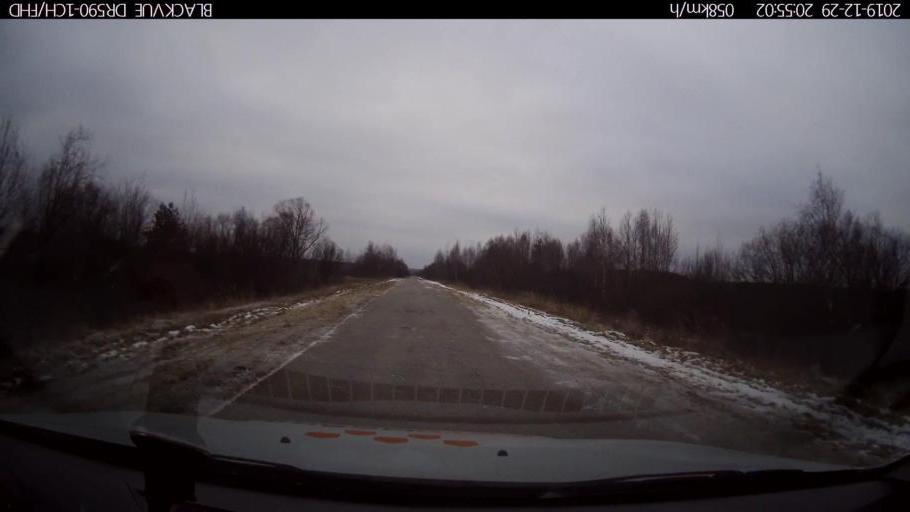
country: RU
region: Nizjnij Novgorod
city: Afonino
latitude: 56.1597
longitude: 43.9922
